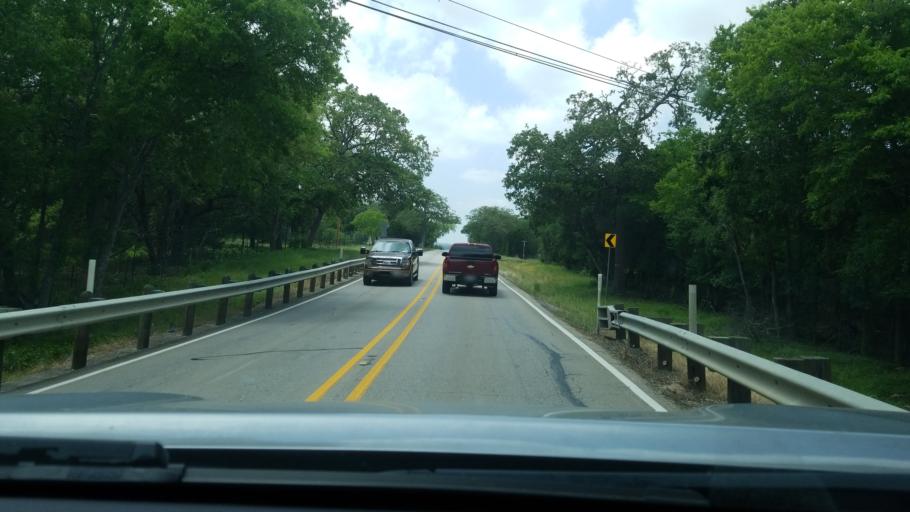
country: US
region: Texas
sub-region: Hays County
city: Dripping Springs
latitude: 30.1596
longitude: -98.0694
